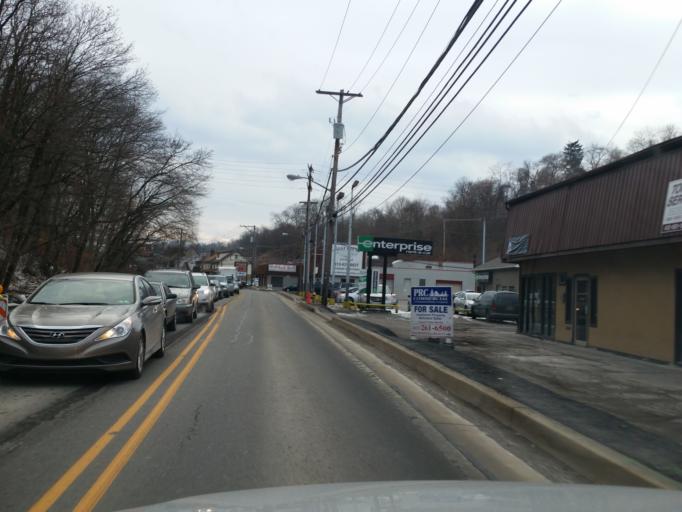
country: US
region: Pennsylvania
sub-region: Allegheny County
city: Whitehall
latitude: 40.3813
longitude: -79.9988
